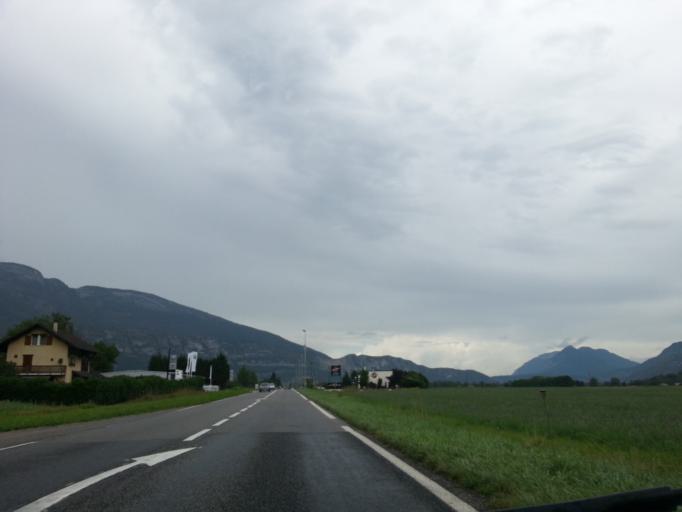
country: FR
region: Rhone-Alpes
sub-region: Departement de la Haute-Savoie
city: Doussard
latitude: 45.7758
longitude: 6.2358
